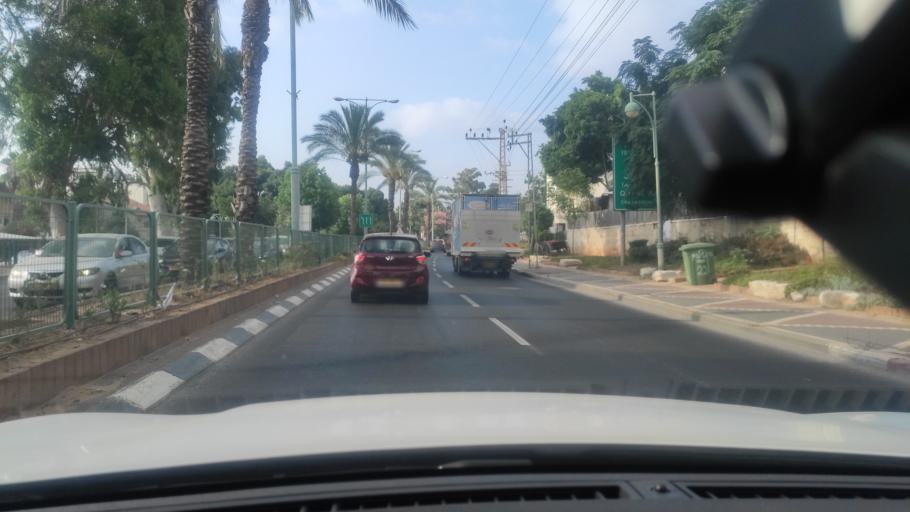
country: IL
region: Central District
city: Petah Tiqwa
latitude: 32.0930
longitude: 34.9021
